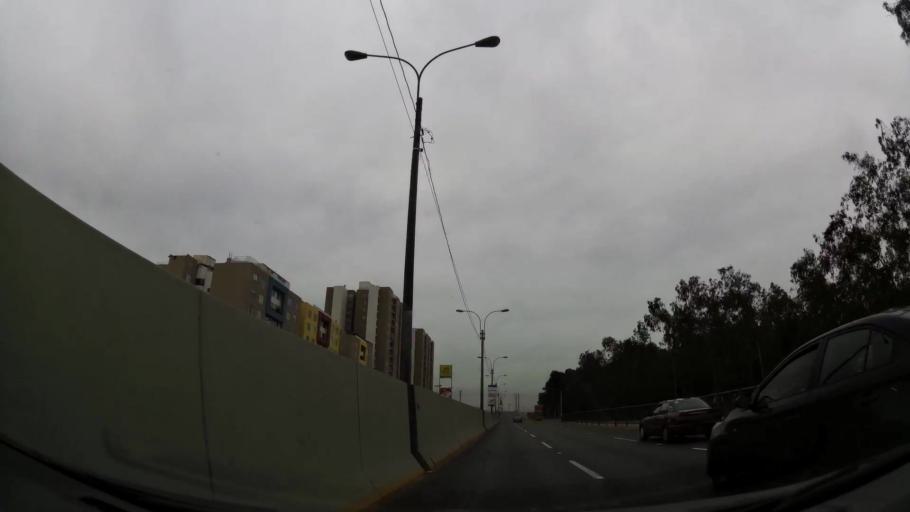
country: PE
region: Callao
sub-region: Callao
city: Callao
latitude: -12.0507
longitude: -77.0816
